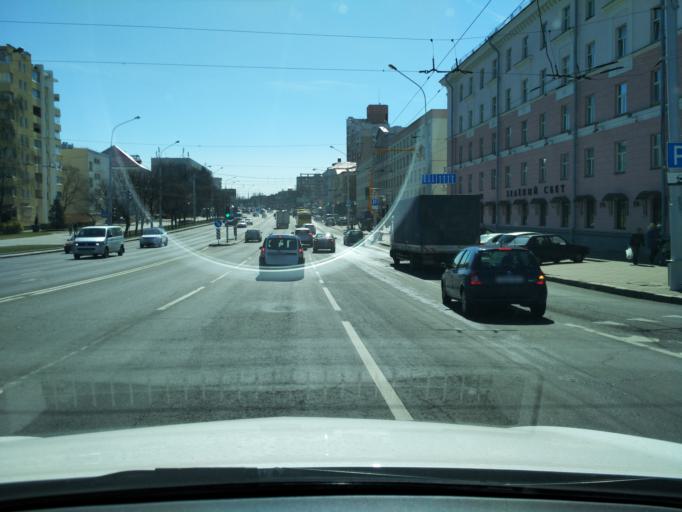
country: BY
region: Minsk
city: Minsk
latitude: 53.8821
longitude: 27.5361
